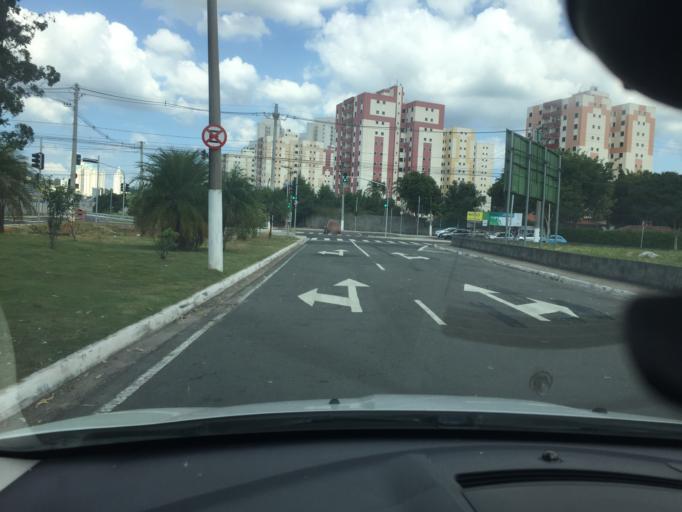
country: BR
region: Sao Paulo
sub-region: Jundiai
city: Jundiai
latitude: -23.1759
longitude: -46.9063
